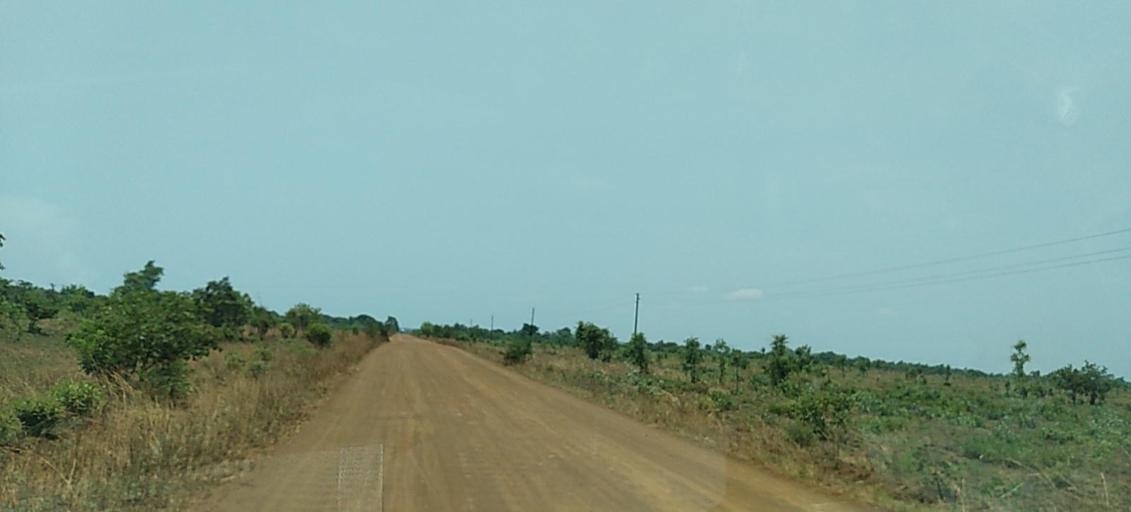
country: ZM
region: Copperbelt
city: Mpongwe
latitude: -13.6824
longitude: 27.8587
